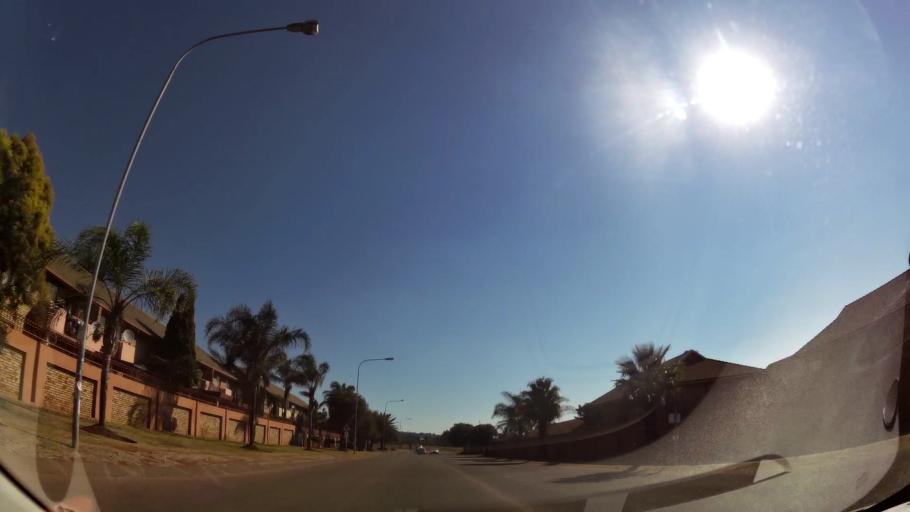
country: ZA
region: Gauteng
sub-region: City of Tshwane Metropolitan Municipality
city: Centurion
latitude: -25.8518
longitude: 28.1804
